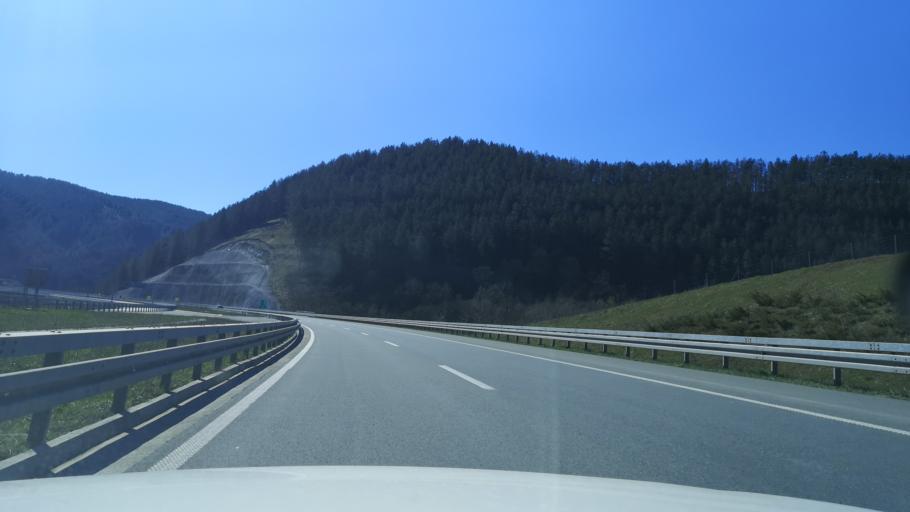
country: RS
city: Prislonica
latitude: 44.0172
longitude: 20.3589
